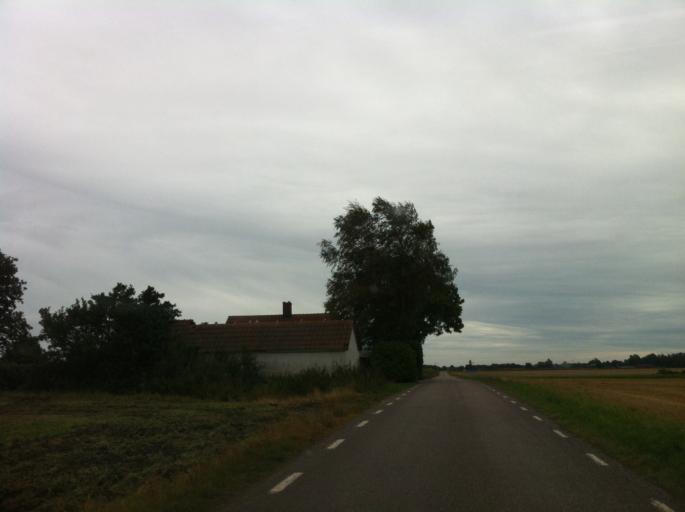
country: SE
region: Skane
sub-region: Landskrona
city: Asmundtorp
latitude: 55.9448
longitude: 12.9931
